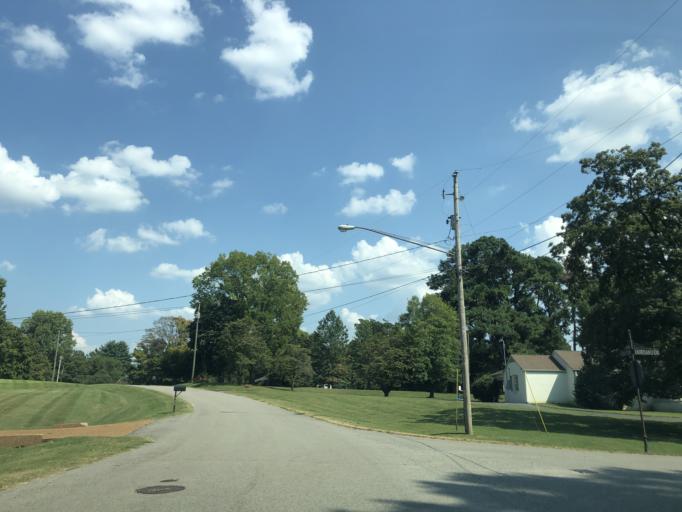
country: US
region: Tennessee
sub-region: Davidson County
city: Oak Hill
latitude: 36.0925
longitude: -86.7682
